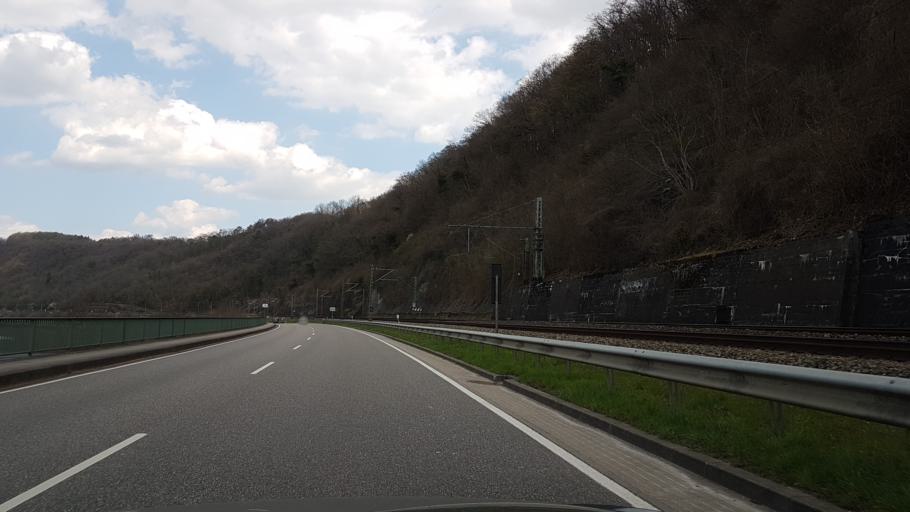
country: DE
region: Baden-Wuerttemberg
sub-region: Karlsruhe Region
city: Hassmersheim
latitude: 49.2949
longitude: 9.1520
